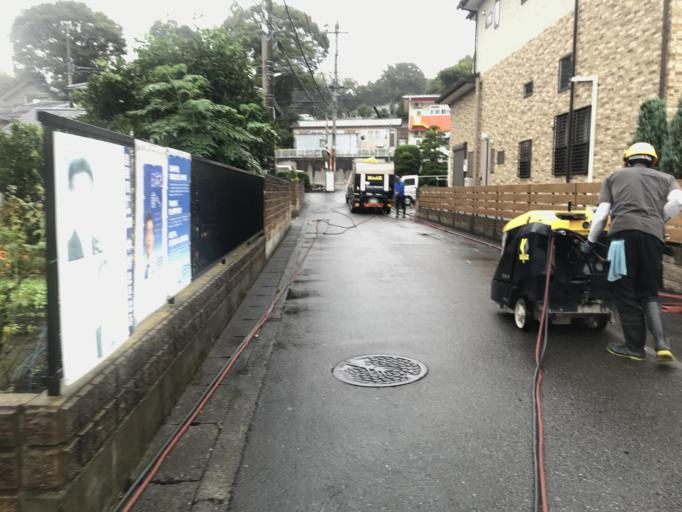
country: JP
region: Kanagawa
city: Zama
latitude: 35.5486
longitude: 139.3265
